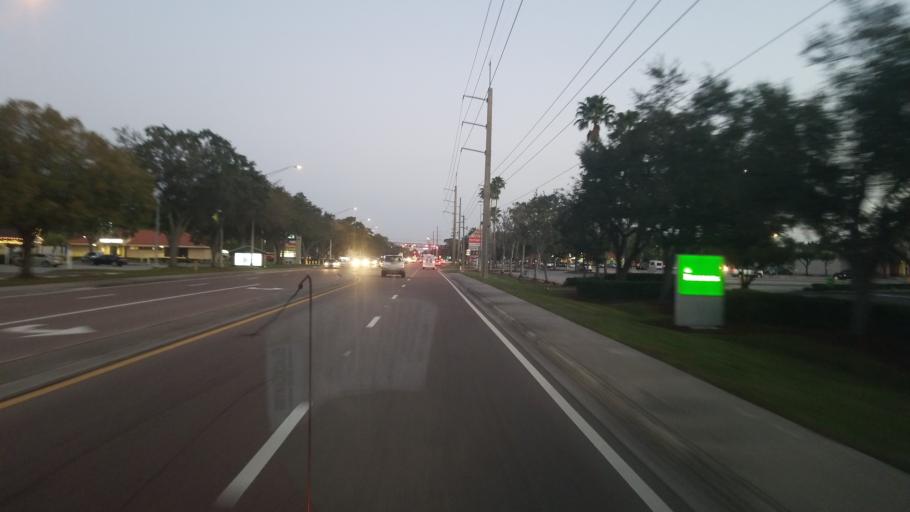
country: US
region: Florida
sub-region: Sarasota County
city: Lake Sarasota
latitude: 27.2960
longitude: -82.4516
